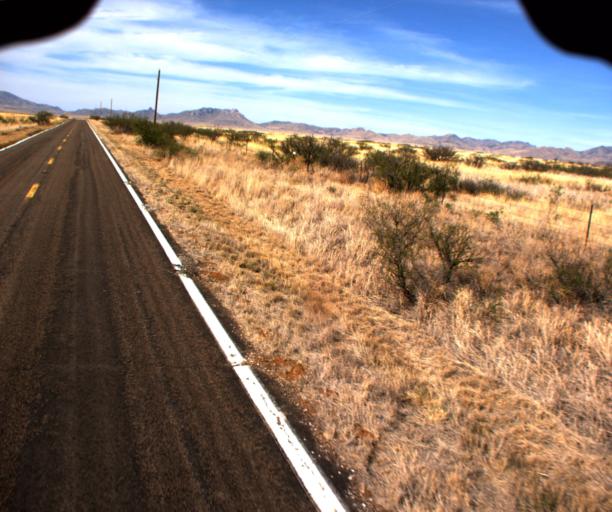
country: US
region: Arizona
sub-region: Cochise County
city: Willcox
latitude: 31.9616
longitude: -109.4771
